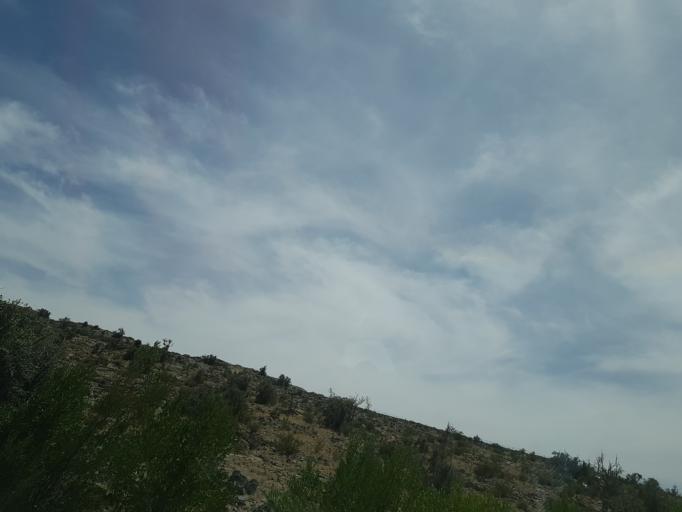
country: OM
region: Al Batinah
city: Bayt al `Awabi
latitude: 23.1410
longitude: 57.5381
